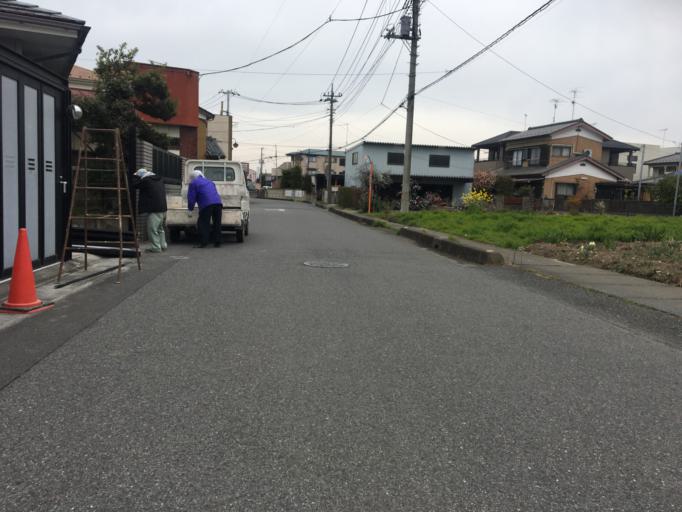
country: JP
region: Saitama
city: Kisai
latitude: 36.1009
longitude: 139.5788
